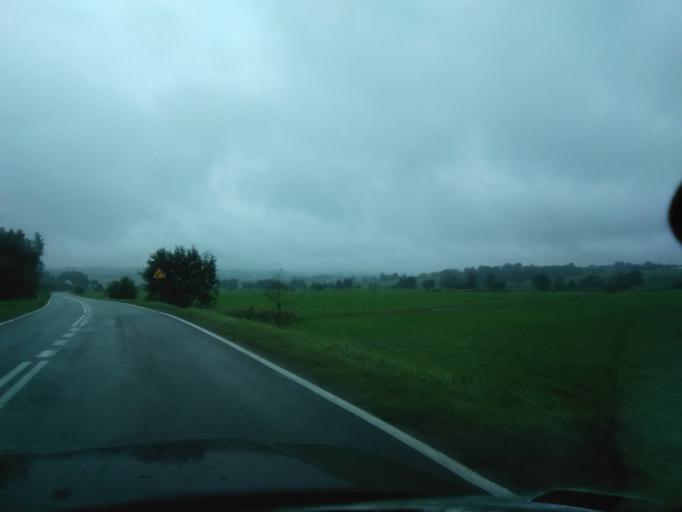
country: PL
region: Subcarpathian Voivodeship
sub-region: Powiat ropczycko-sedziszowski
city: Niedzwiada
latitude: 49.9884
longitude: 21.5616
